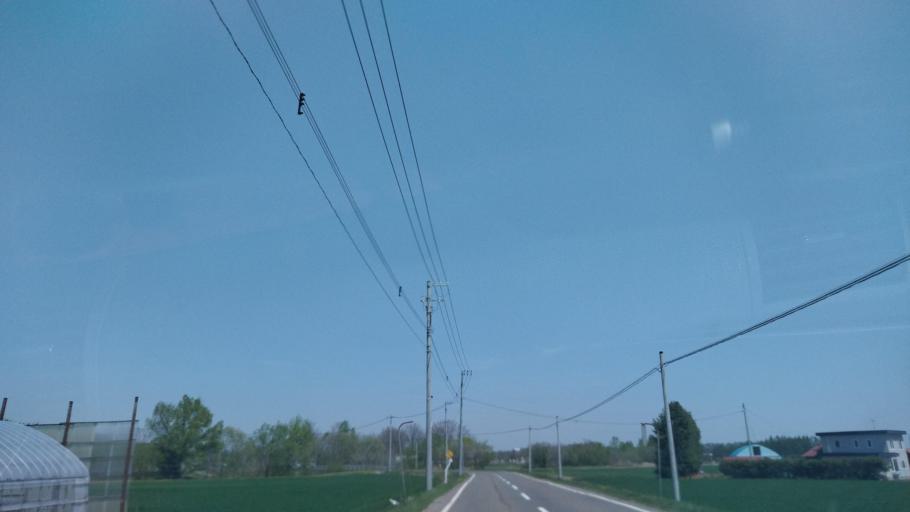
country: JP
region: Hokkaido
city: Obihiro
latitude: 42.8922
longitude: 143.0286
